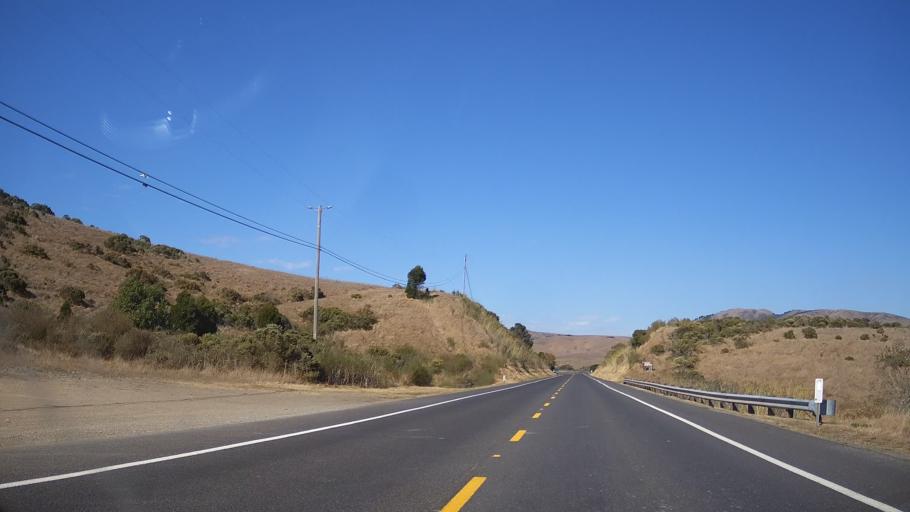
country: US
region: California
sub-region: Marin County
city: Lagunitas-Forest Knolls
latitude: 38.0820
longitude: -122.7537
